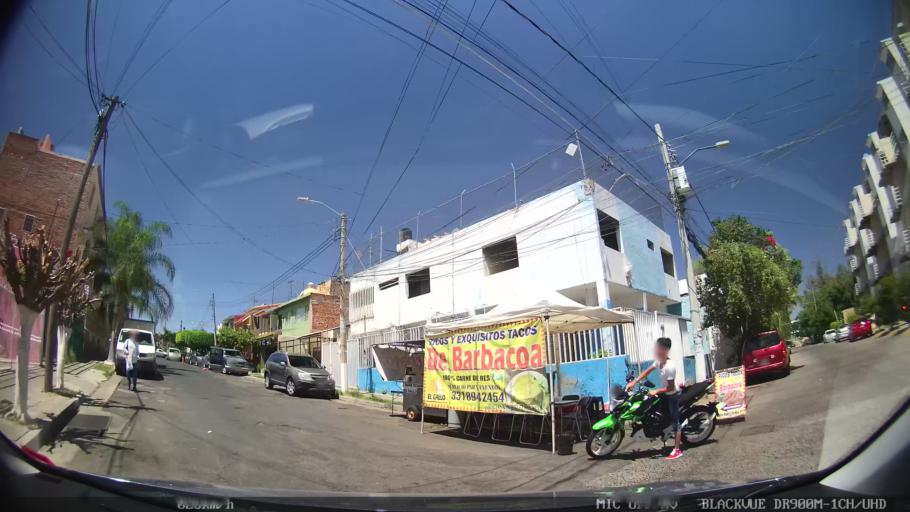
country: MX
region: Jalisco
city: Tlaquepaque
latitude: 20.6811
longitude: -103.2914
